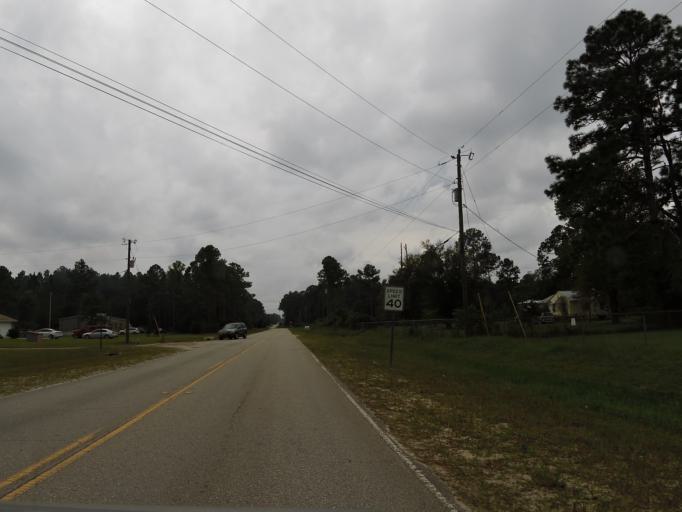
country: US
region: Florida
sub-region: Clay County
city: Middleburg
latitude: 30.1236
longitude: -81.9493
